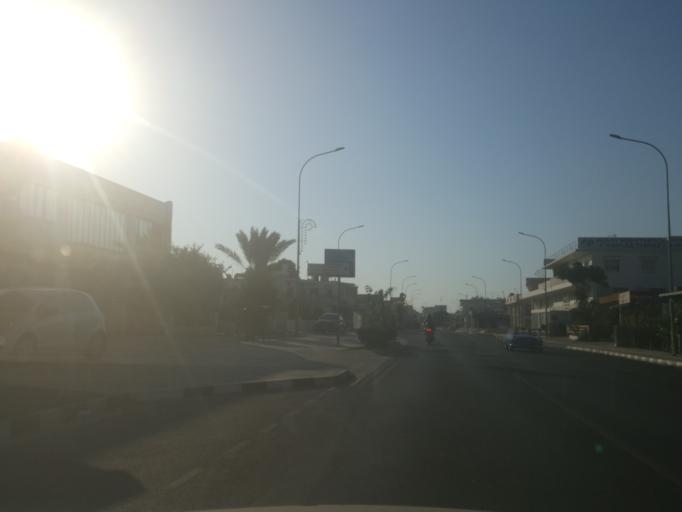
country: CY
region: Ammochostos
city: Deryneia
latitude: 35.0585
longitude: 33.9675
